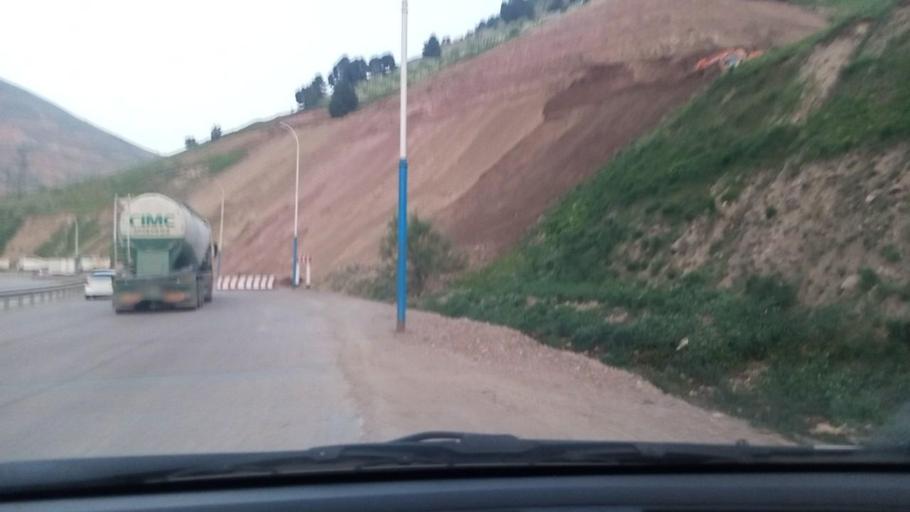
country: UZ
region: Toshkent
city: Angren
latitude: 41.1067
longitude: 70.4983
